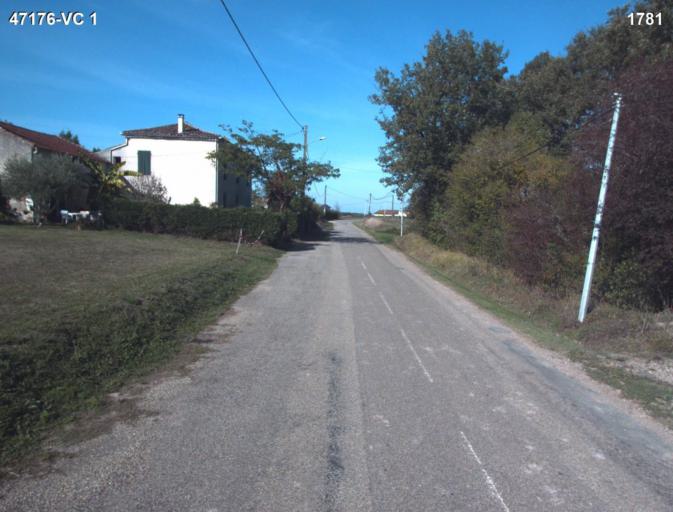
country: FR
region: Aquitaine
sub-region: Departement du Lot-et-Garonne
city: Vianne
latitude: 44.2085
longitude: 0.2945
